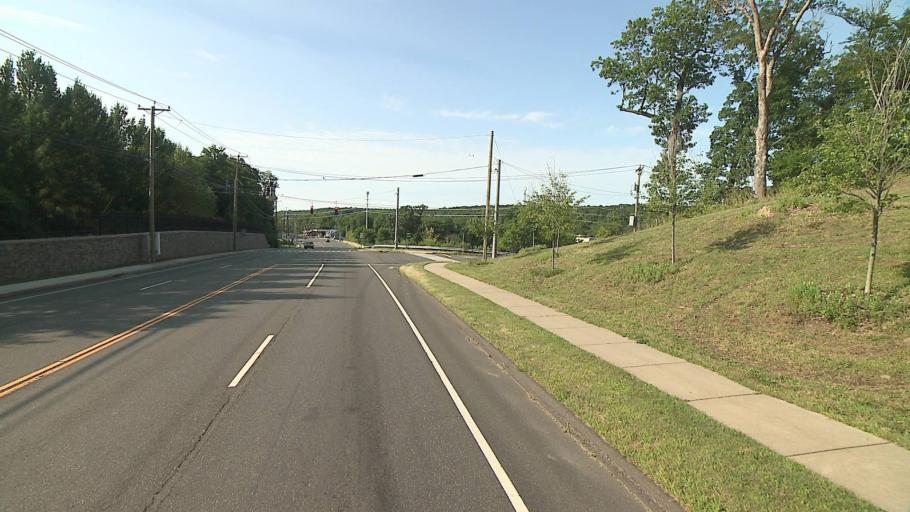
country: US
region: Connecticut
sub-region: Fairfield County
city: Wilton
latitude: 41.1983
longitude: -73.4311
